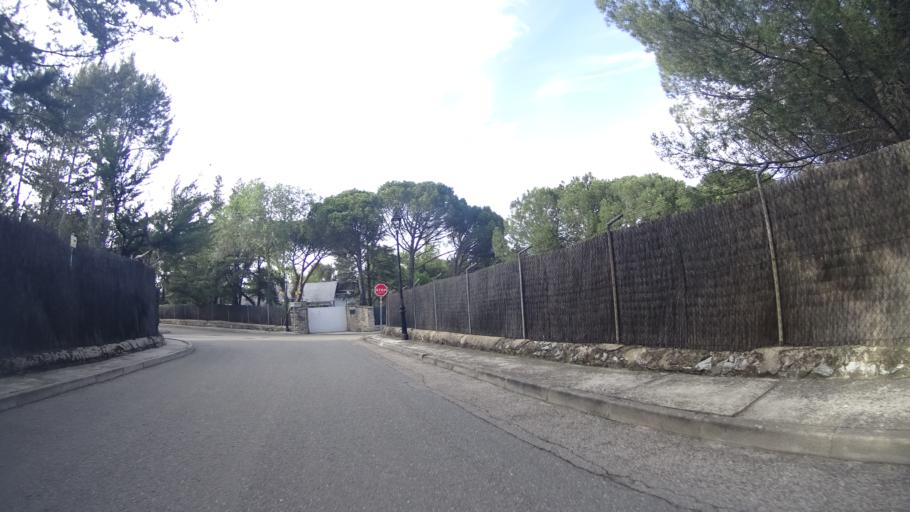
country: ES
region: Madrid
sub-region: Provincia de Madrid
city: Galapagar
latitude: 40.5845
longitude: -3.9691
